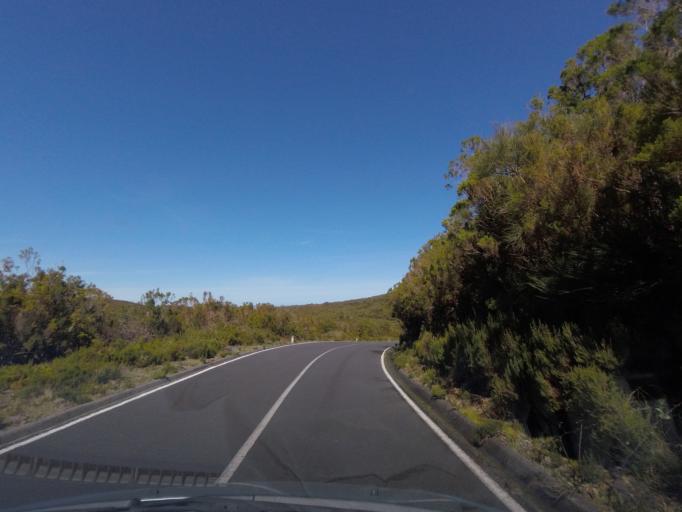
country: PT
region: Madeira
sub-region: Porto Moniz
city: Porto Moniz
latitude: 32.7960
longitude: -17.1314
